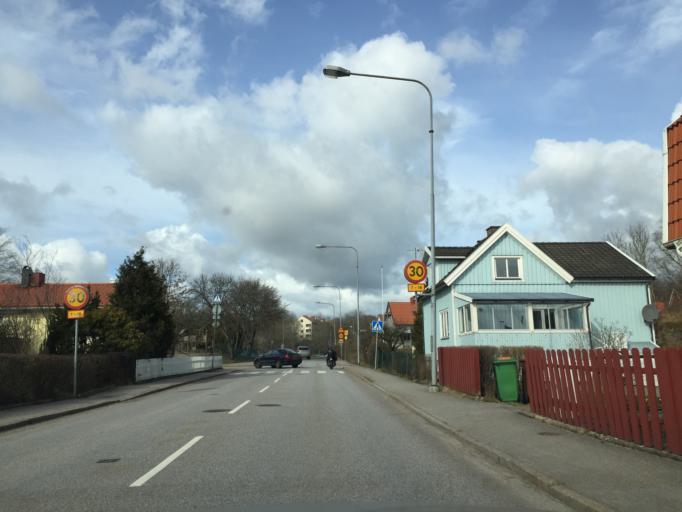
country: SE
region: Vaestra Goetaland
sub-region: Uddevalla Kommun
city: Uddevalla
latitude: 58.3602
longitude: 11.9396
